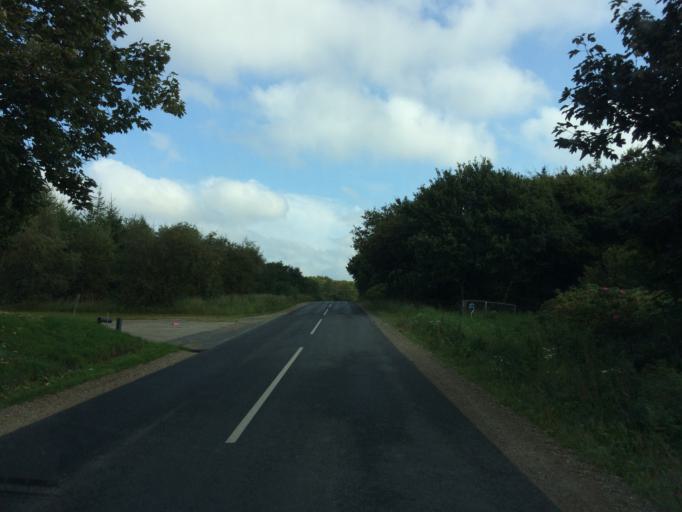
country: DK
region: Central Jutland
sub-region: Holstebro Kommune
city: Vinderup
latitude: 56.4625
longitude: 8.8842
